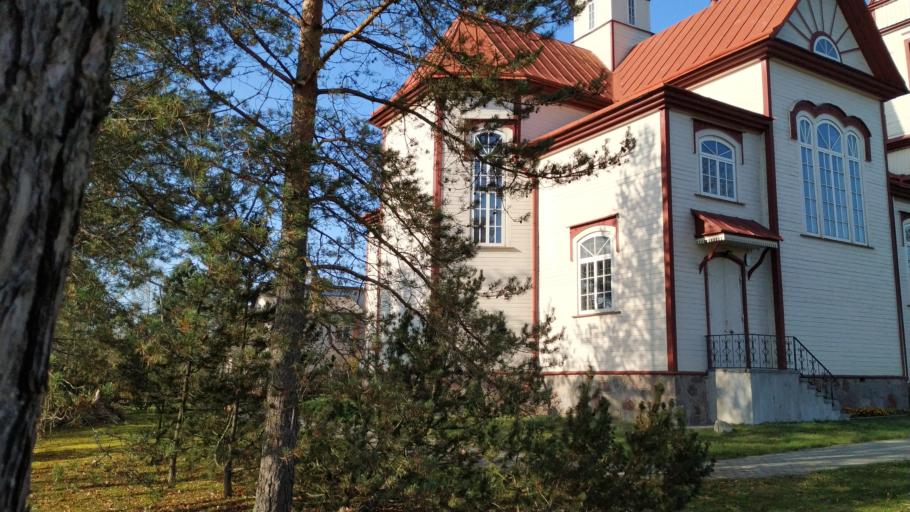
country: LT
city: Aukstadvaris
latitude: 54.5780
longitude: 24.5348
